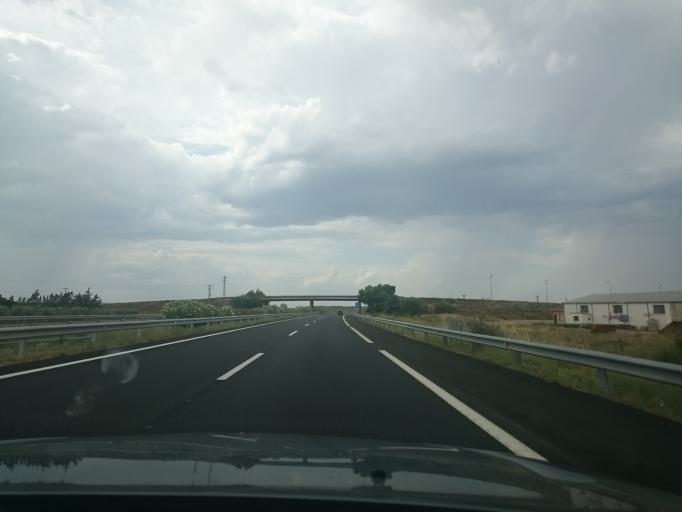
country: ES
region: La Rioja
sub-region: Provincia de La Rioja
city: Aldeanueva de Ebro
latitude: 42.2240
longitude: -1.8969
